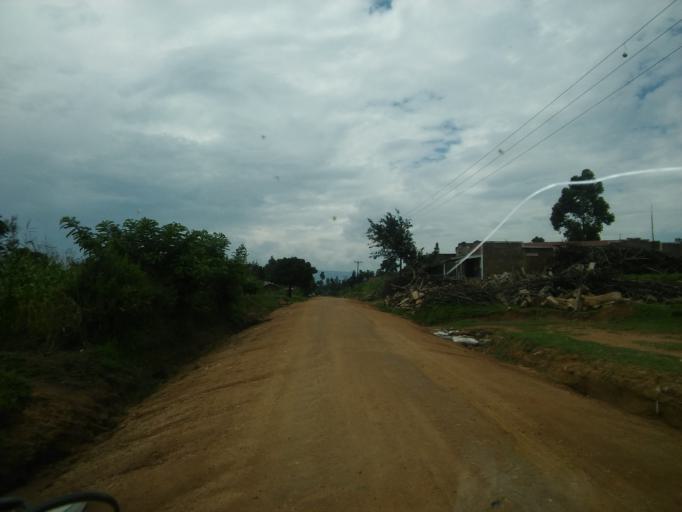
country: KE
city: Malikisi
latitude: 0.8173
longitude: 34.3489
